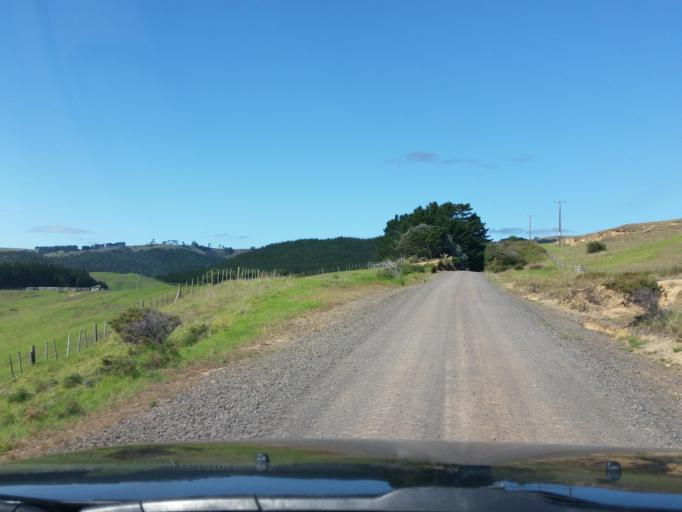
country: NZ
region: Northland
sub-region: Kaipara District
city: Dargaville
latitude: -35.7045
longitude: 173.5327
